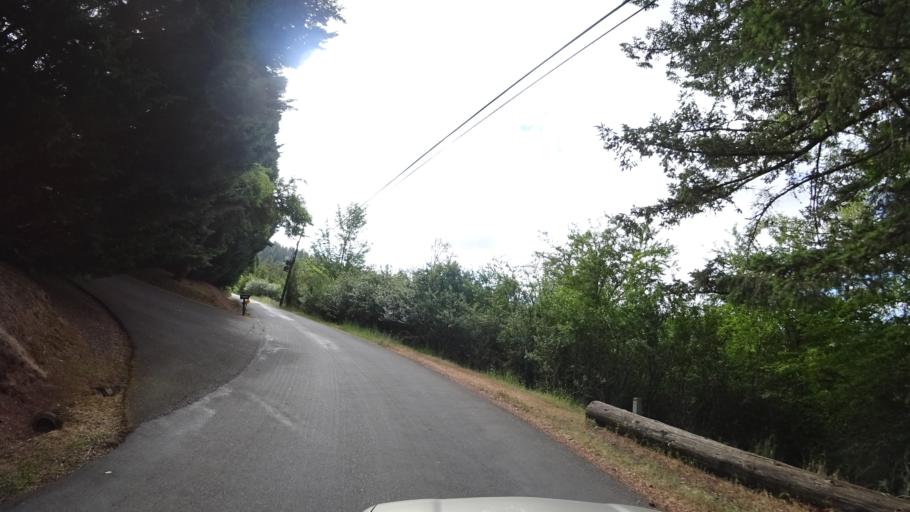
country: US
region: Oregon
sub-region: Washington County
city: Oak Hills
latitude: 45.5803
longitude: -122.8224
